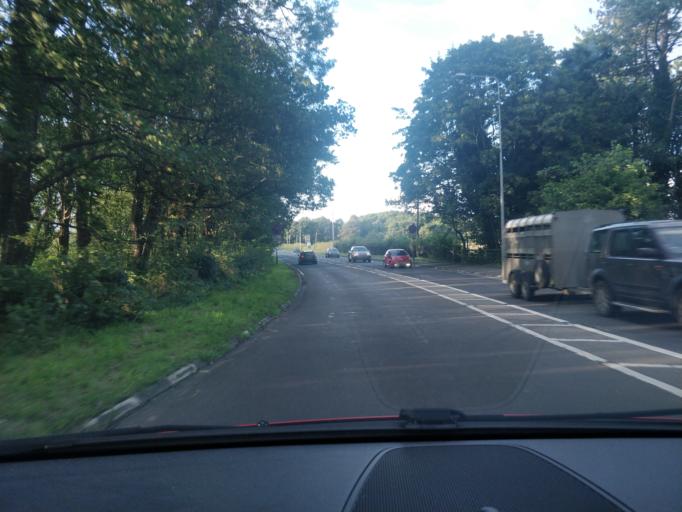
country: GB
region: England
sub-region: Lancashire
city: Tarleton
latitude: 53.6765
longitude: -2.8178
